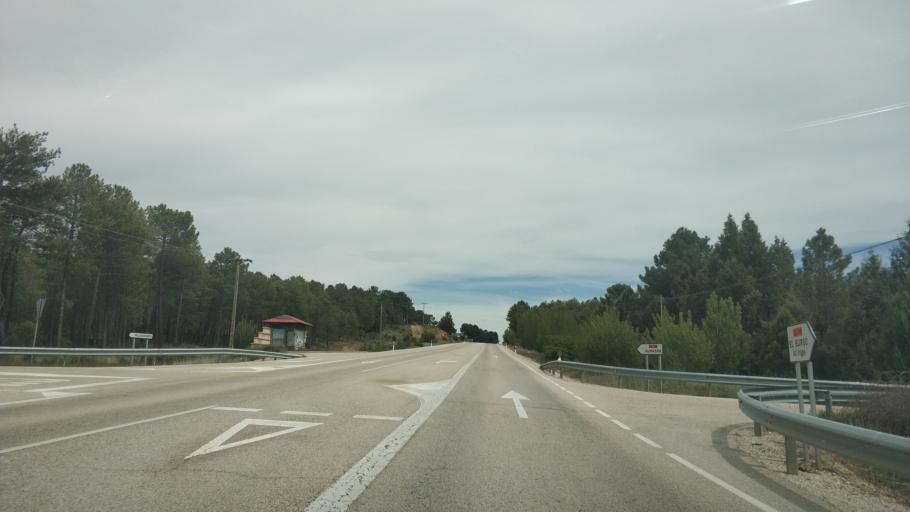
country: ES
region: Castille and Leon
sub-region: Provincia de Soria
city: Valdenebro
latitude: 41.5601
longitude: -2.9736
